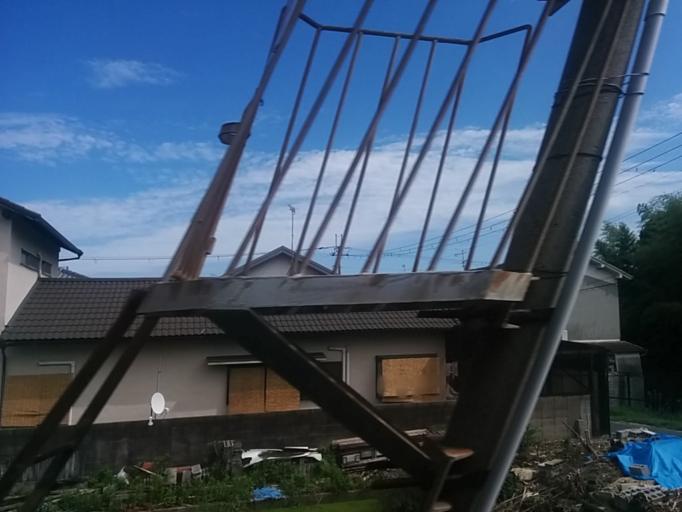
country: JP
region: Nara
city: Nara-shi
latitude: 34.6571
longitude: 135.7826
